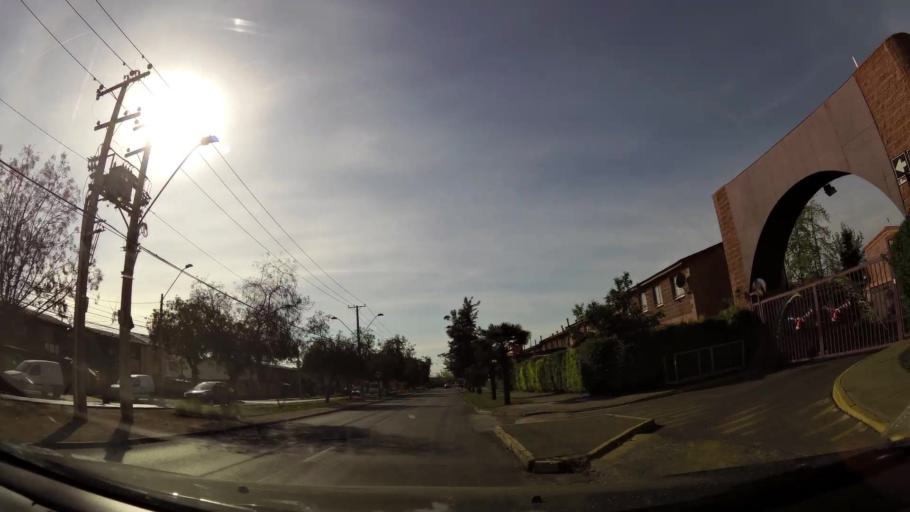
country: CL
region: Santiago Metropolitan
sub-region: Provincia de Cordillera
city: Puente Alto
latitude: -33.5896
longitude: -70.5619
